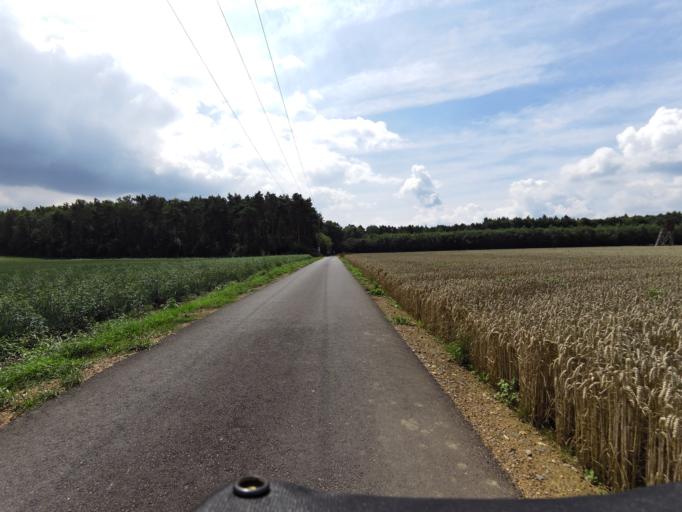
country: DE
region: North Rhine-Westphalia
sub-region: Regierungsbezirk Dusseldorf
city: Niederkruchten
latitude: 51.1835
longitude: 6.1972
